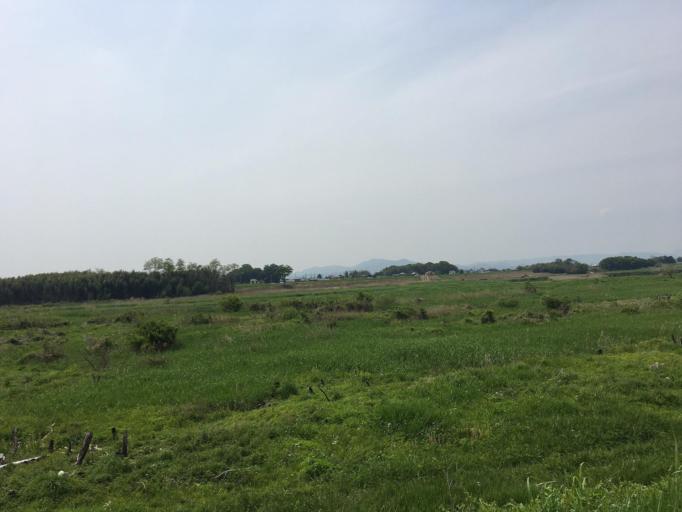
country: JP
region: Tochigi
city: Mibu
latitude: 36.3602
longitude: 139.8070
